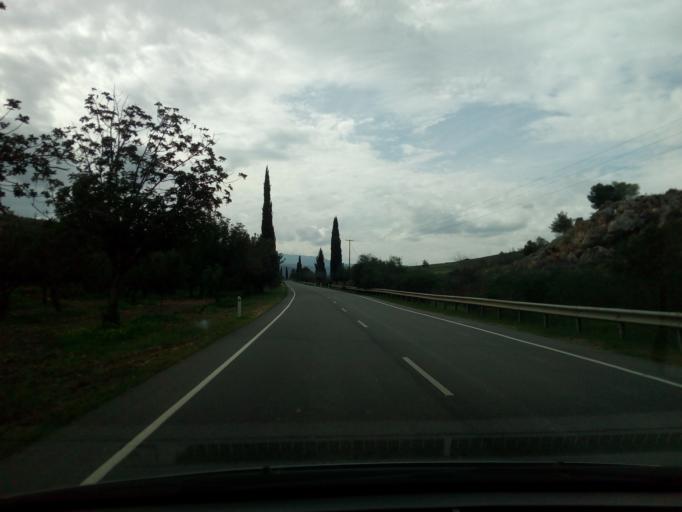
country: CY
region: Lefkosia
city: Astromeritis
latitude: 35.0937
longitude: 32.9657
